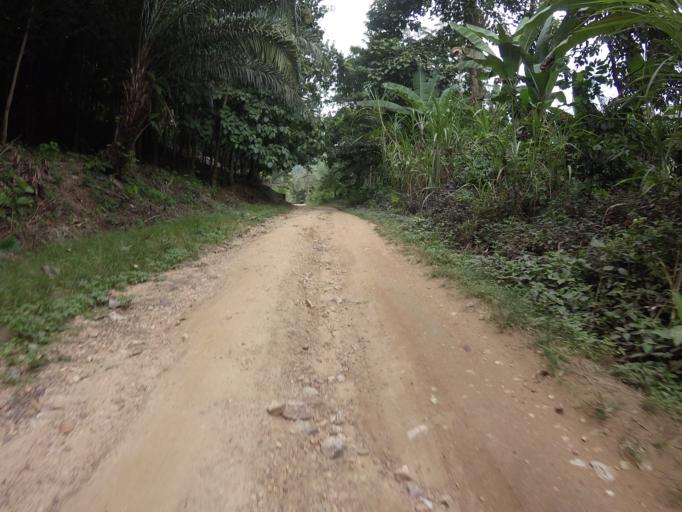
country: GH
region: Volta
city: Kpandu
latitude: 6.8786
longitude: 0.4410
